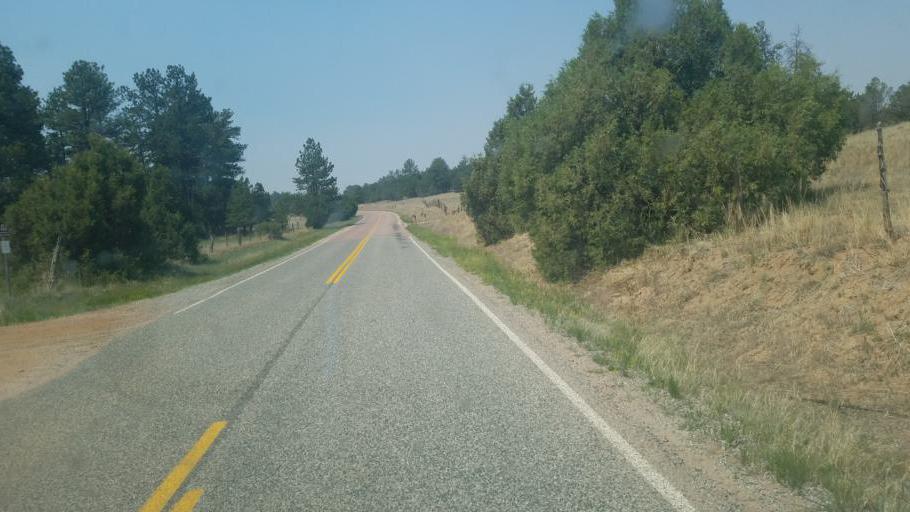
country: US
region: Colorado
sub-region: Custer County
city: Westcliffe
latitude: 38.3641
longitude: -105.4658
